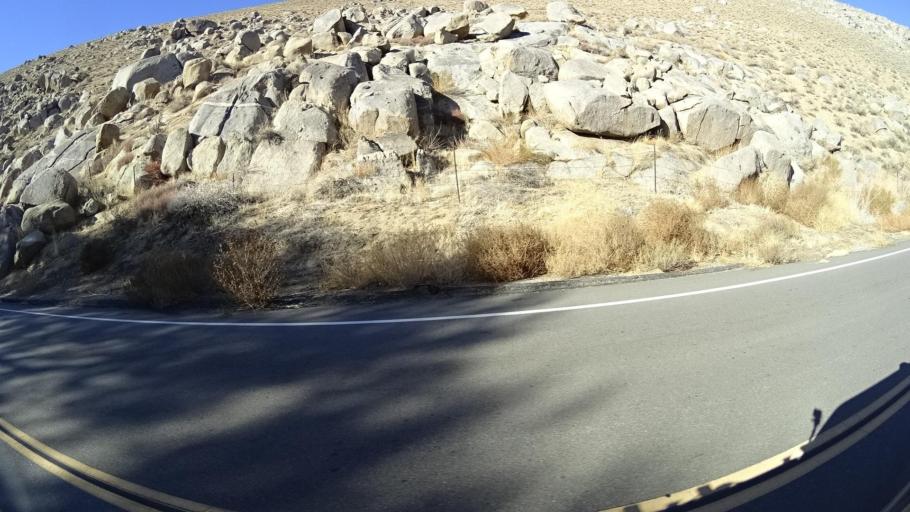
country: US
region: California
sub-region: Kern County
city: Weldon
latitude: 35.6722
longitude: -118.3329
